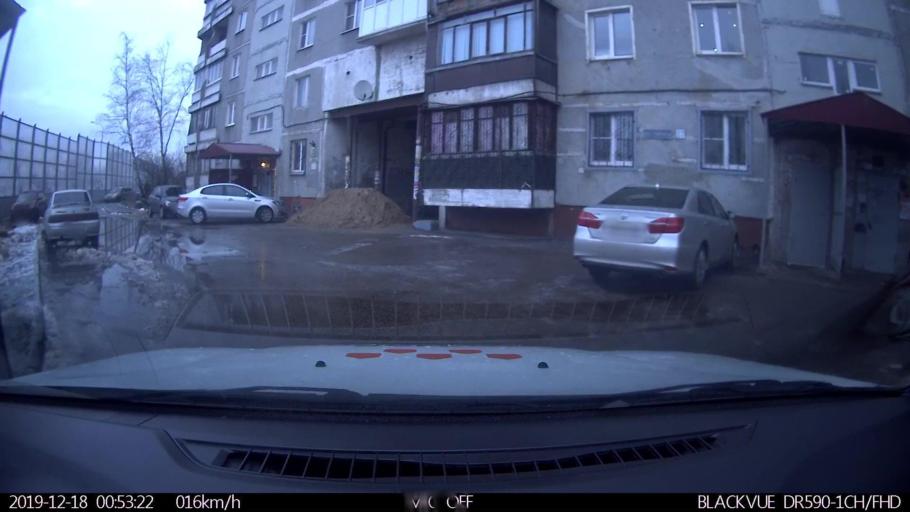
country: RU
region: Nizjnij Novgorod
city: Nizhniy Novgorod
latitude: 56.3419
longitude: 43.9230
